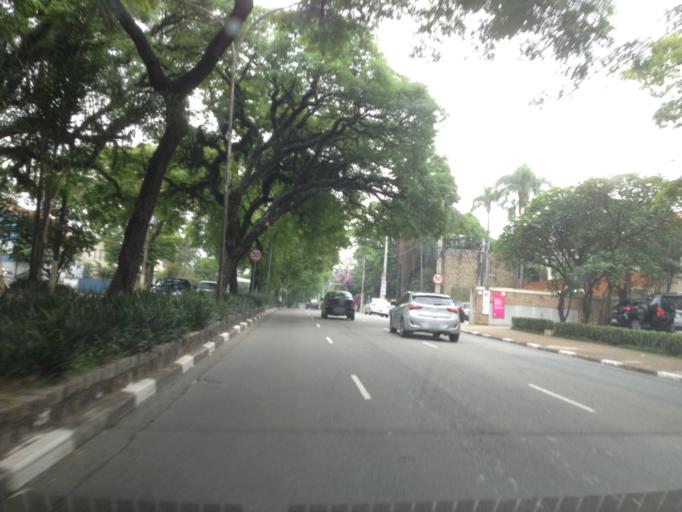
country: BR
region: Sao Paulo
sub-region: Sao Paulo
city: Sao Paulo
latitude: -23.5866
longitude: -46.6640
